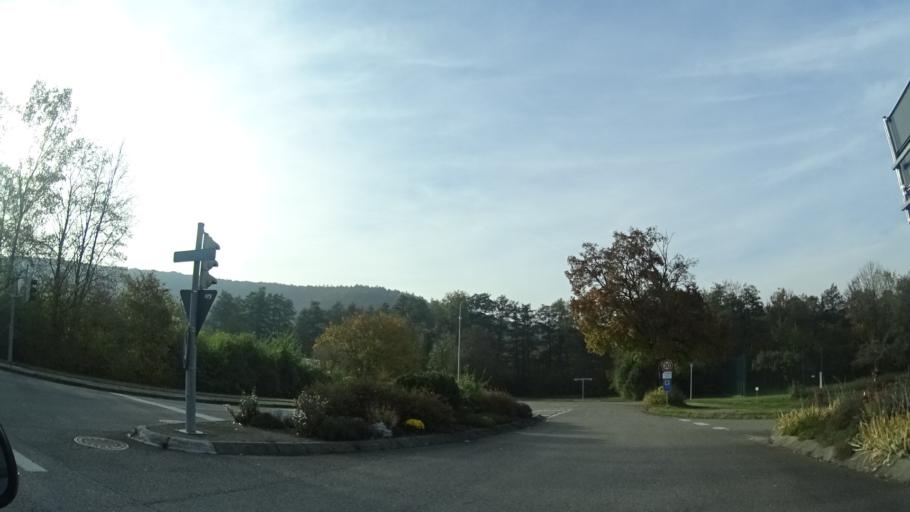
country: DE
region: Baden-Wuerttemberg
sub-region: Karlsruhe Region
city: Mosbach
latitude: 49.3661
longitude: 9.1524
